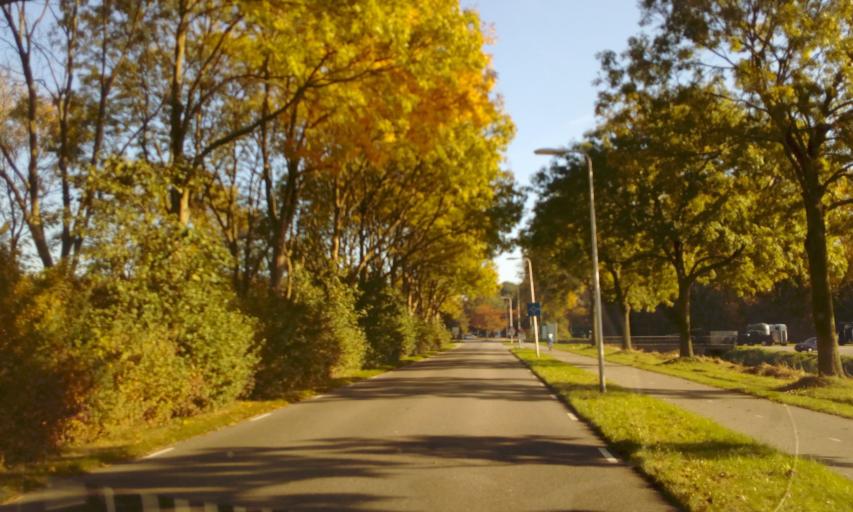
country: NL
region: South Holland
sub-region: Gemeente Lansingerland
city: Bleiswijk
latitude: 52.0002
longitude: 4.5417
